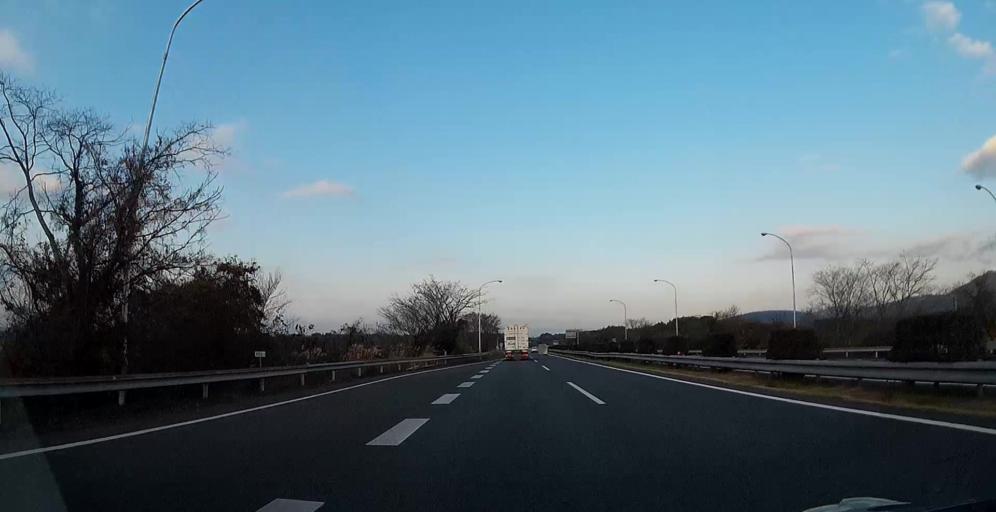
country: JP
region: Kumamoto
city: Kumamoto
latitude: 32.7350
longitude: 130.7778
